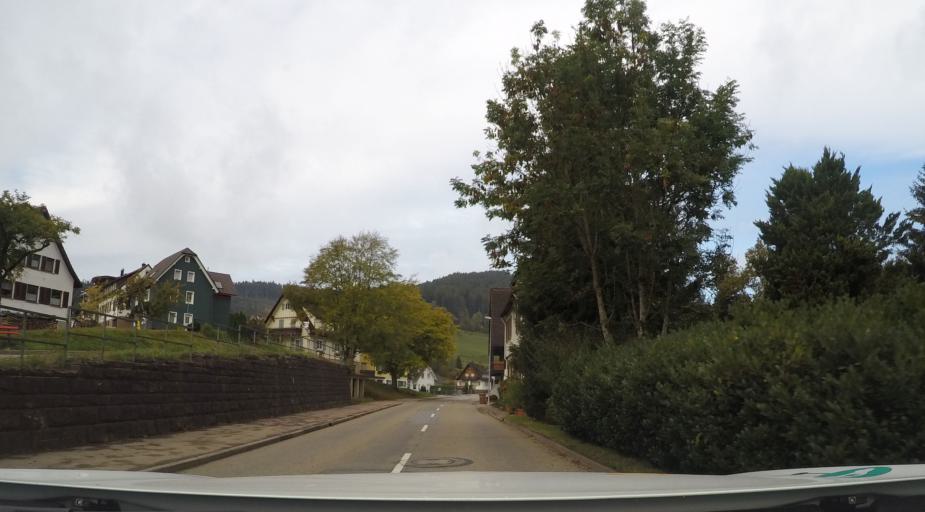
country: DE
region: Baden-Wuerttemberg
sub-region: Karlsruhe Region
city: Baiersbronn
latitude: 48.5232
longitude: 8.3682
